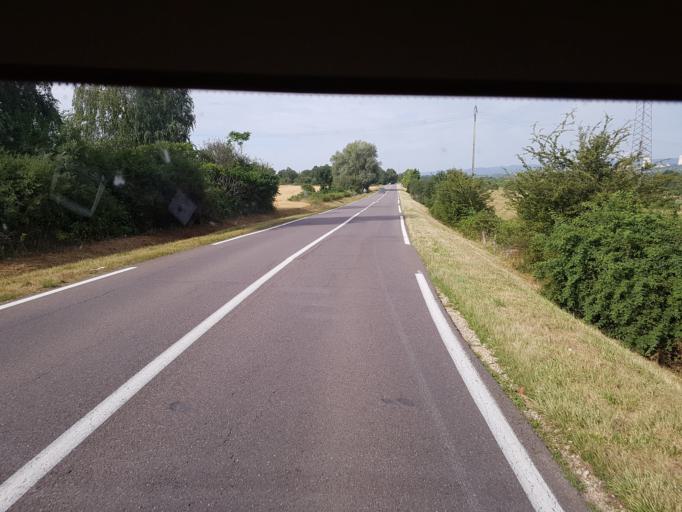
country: FR
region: Lorraine
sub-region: Departement de la Moselle
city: Sierck-les-Bains
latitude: 49.4220
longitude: 6.3259
